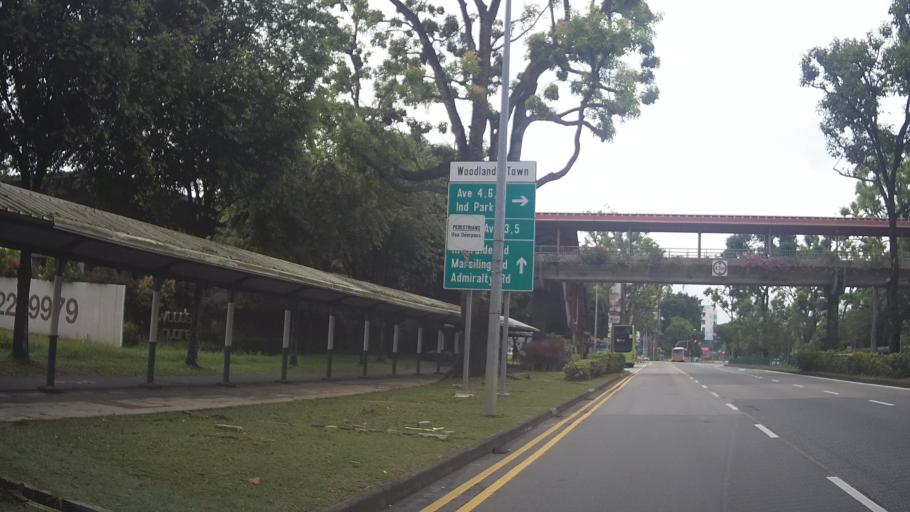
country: MY
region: Johor
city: Johor Bahru
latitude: 1.4400
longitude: 103.7868
